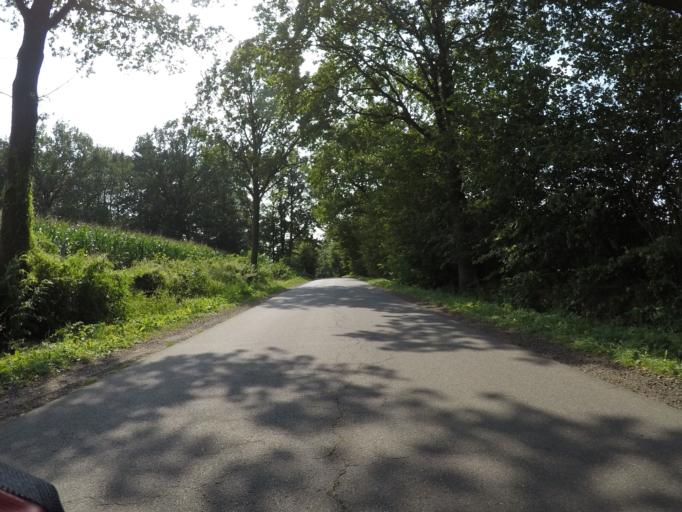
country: DE
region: Schleswig-Holstein
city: Henstedt-Ulzburg
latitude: 53.7732
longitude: 10.0194
